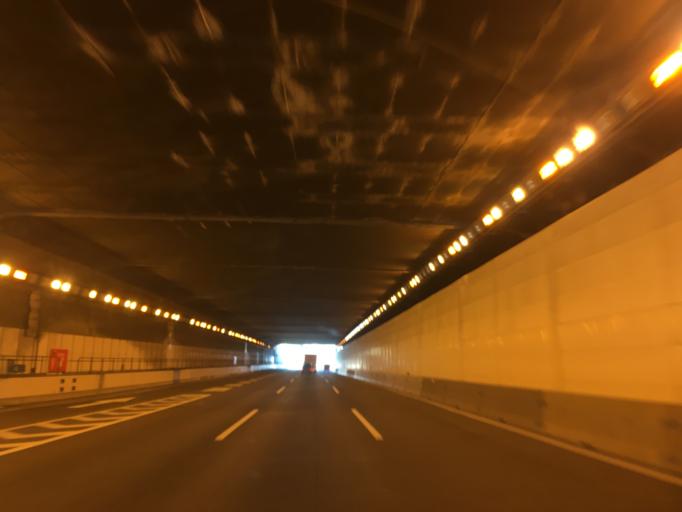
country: JP
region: Saitama
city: Wako
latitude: 35.7910
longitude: 139.6154
